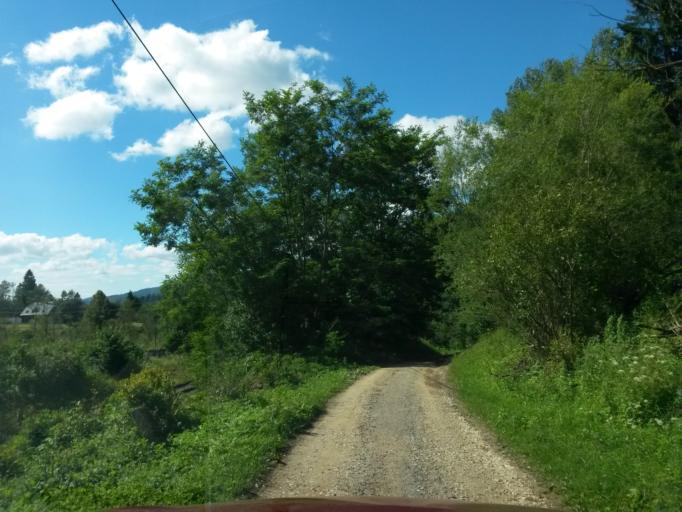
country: SK
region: Kosicky
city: Medzev
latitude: 48.7953
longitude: 20.7520
